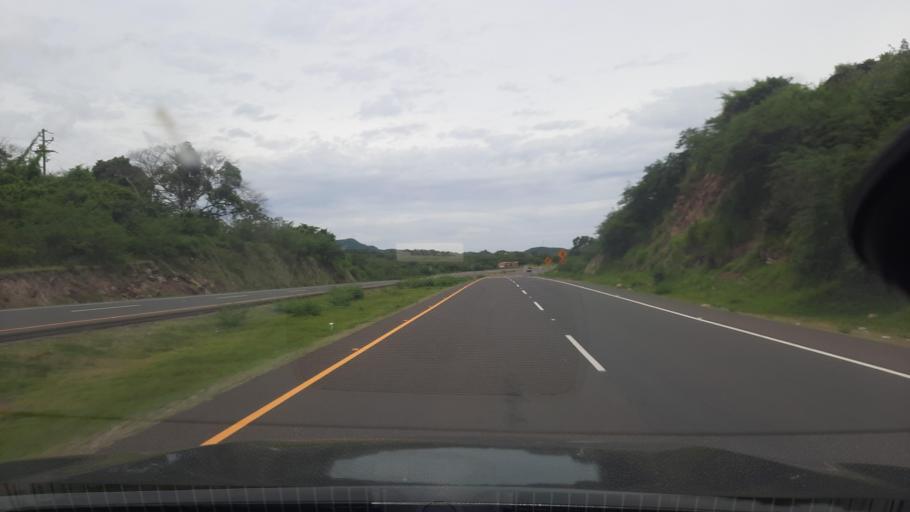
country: HN
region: Valle
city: Aramecina
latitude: 13.7124
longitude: -87.7062
